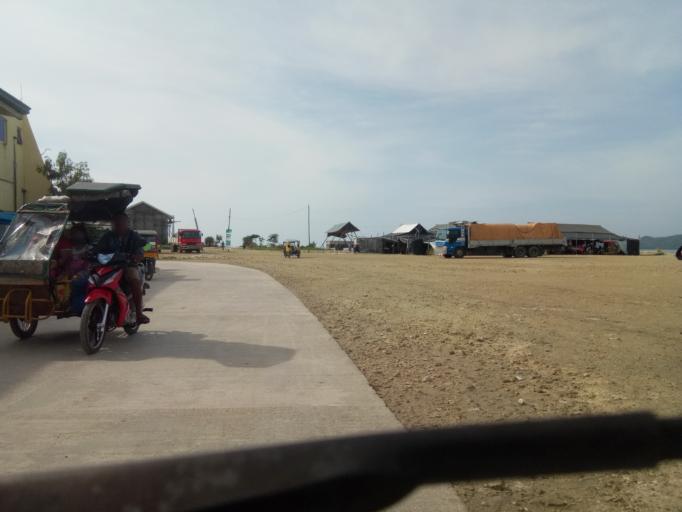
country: PH
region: Caraga
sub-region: Province of Surigao del Norte
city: Dapa
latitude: 9.7549
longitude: 126.0515
